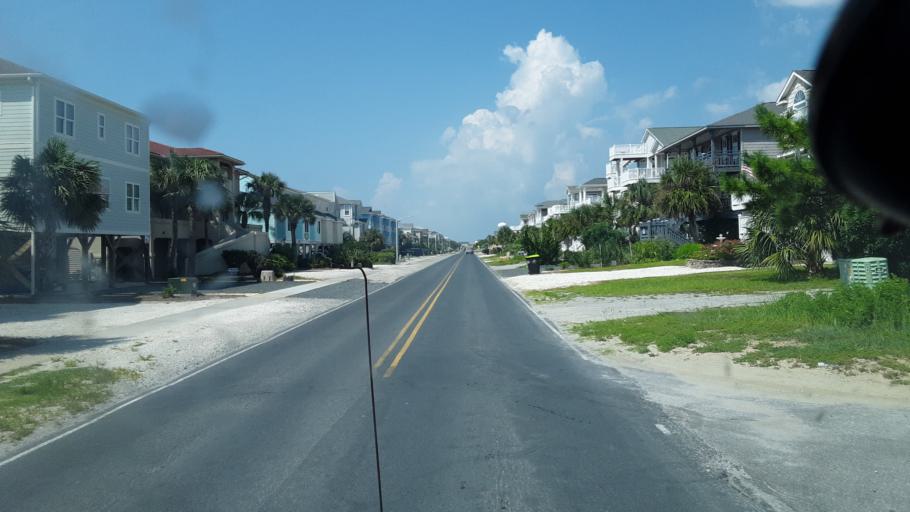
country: US
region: North Carolina
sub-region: Brunswick County
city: Sunset Beach
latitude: 33.8859
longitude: -78.4432
